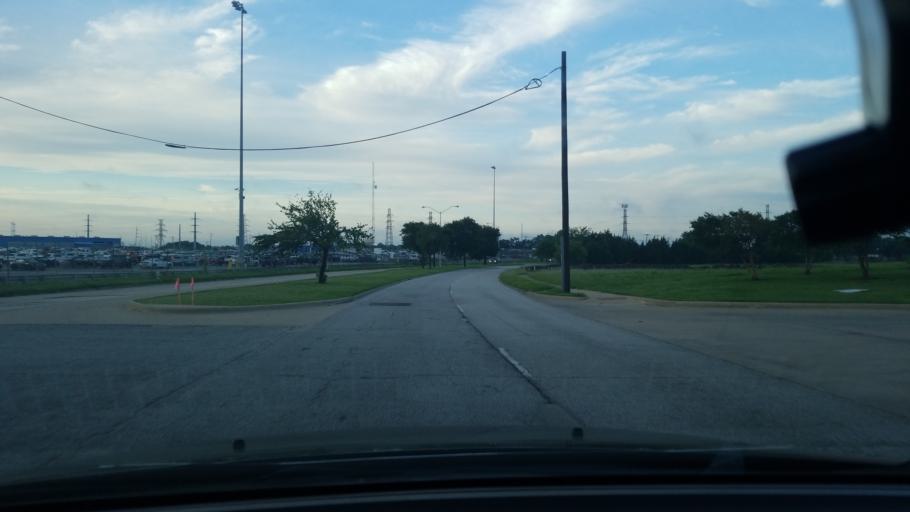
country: US
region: Texas
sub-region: Dallas County
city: Balch Springs
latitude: 32.7813
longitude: -96.6660
